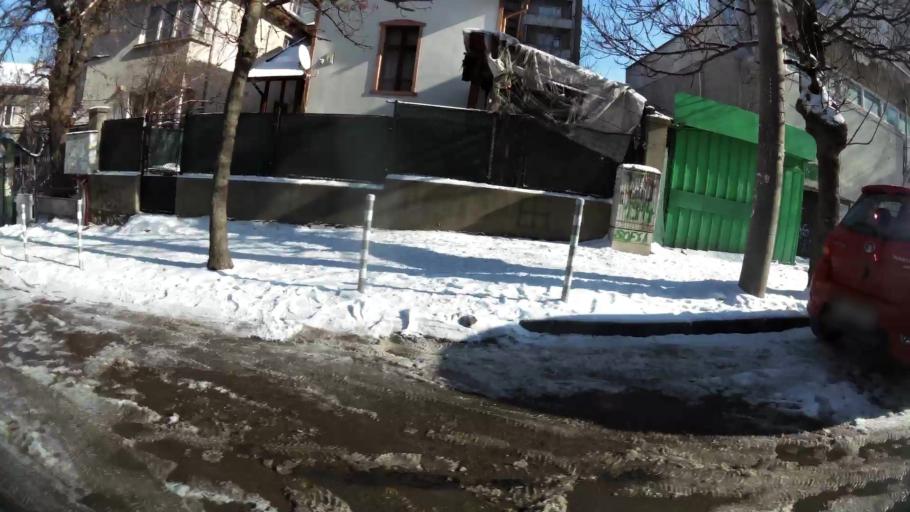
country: BG
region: Sofia-Capital
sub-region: Stolichna Obshtina
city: Sofia
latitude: 42.6772
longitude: 23.3333
